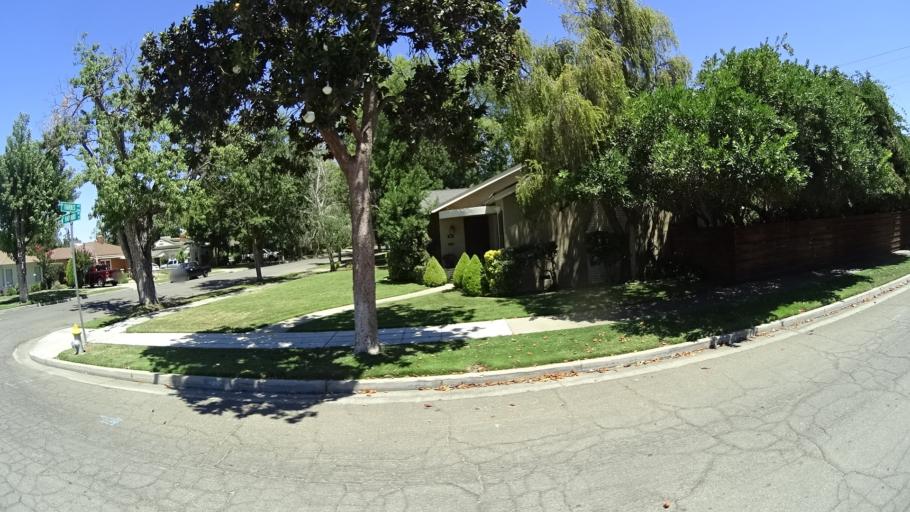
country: US
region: California
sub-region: Fresno County
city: Fresno
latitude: 36.7740
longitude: -119.8119
